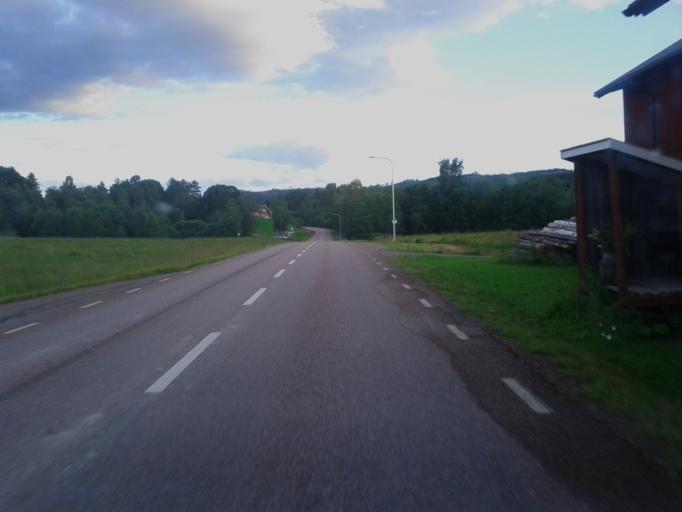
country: SE
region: Dalarna
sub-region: Borlange Kommun
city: Borlaenge
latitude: 60.3899
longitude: 15.3790
